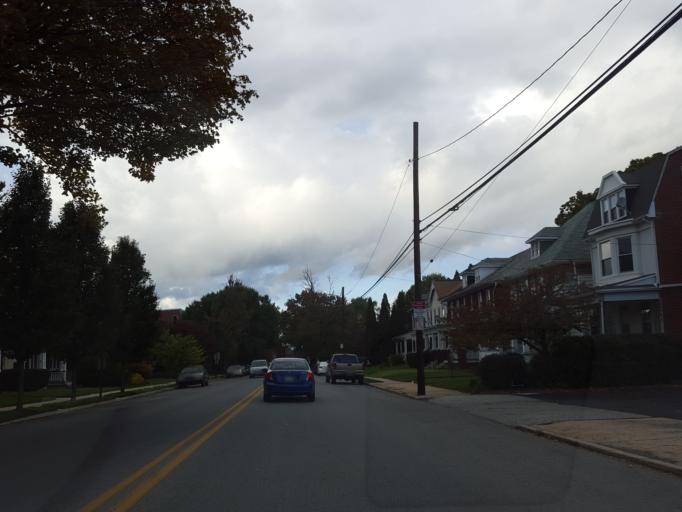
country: US
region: Pennsylvania
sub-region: York County
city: York
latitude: 39.9523
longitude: -76.7165
